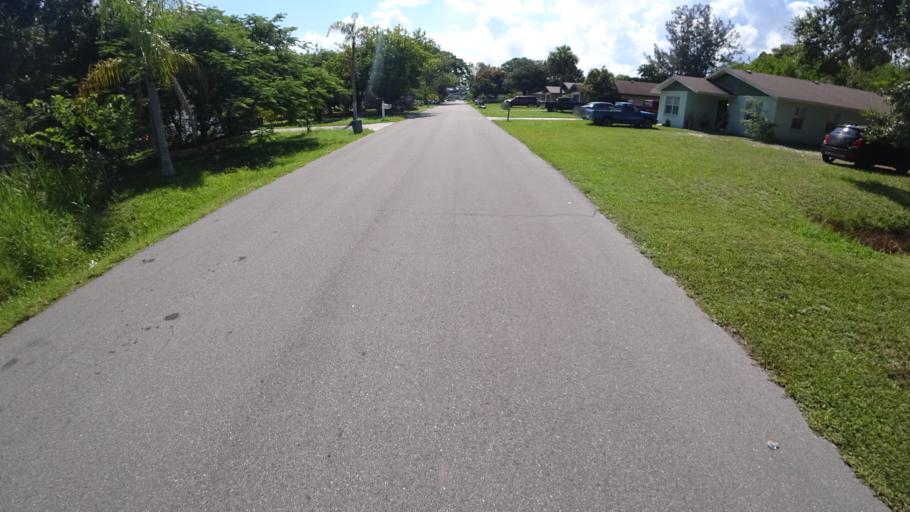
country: US
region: Florida
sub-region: Manatee County
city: Whitfield
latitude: 27.4266
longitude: -82.5569
